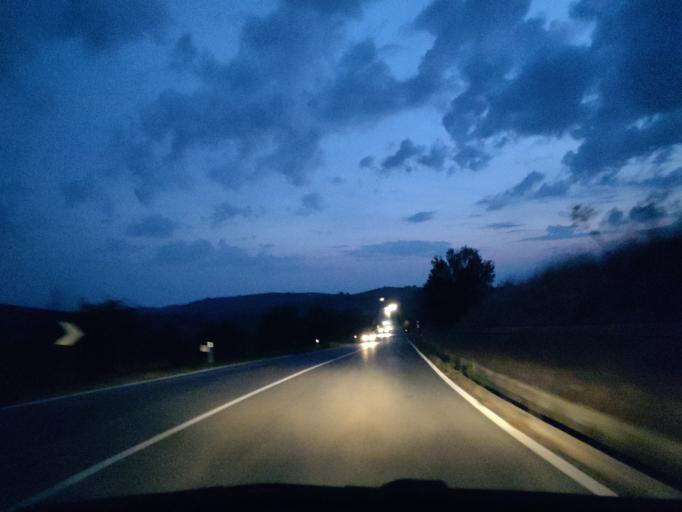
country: IT
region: Latium
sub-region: Provincia di Viterbo
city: Tarquinia
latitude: 42.2569
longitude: 11.8183
